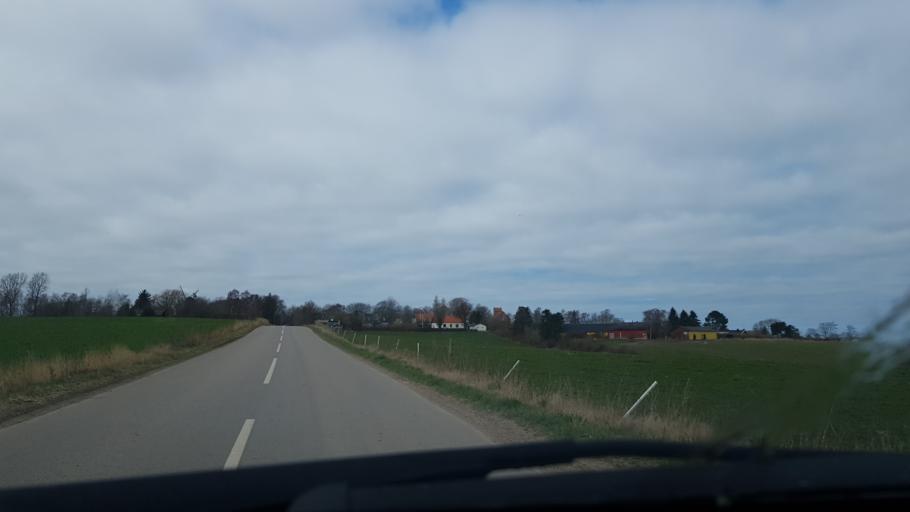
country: DK
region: Zealand
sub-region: Odsherred Kommune
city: Hojby
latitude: 55.9387
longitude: 11.5226
